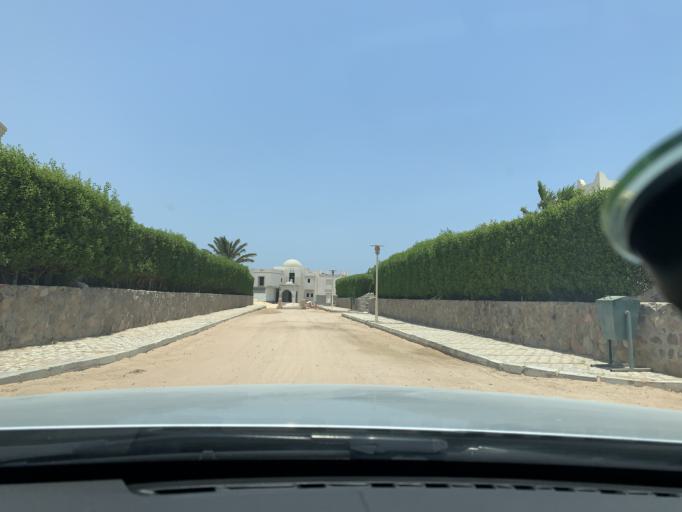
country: EG
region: Red Sea
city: El Gouna
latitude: 27.4173
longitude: 33.6665
